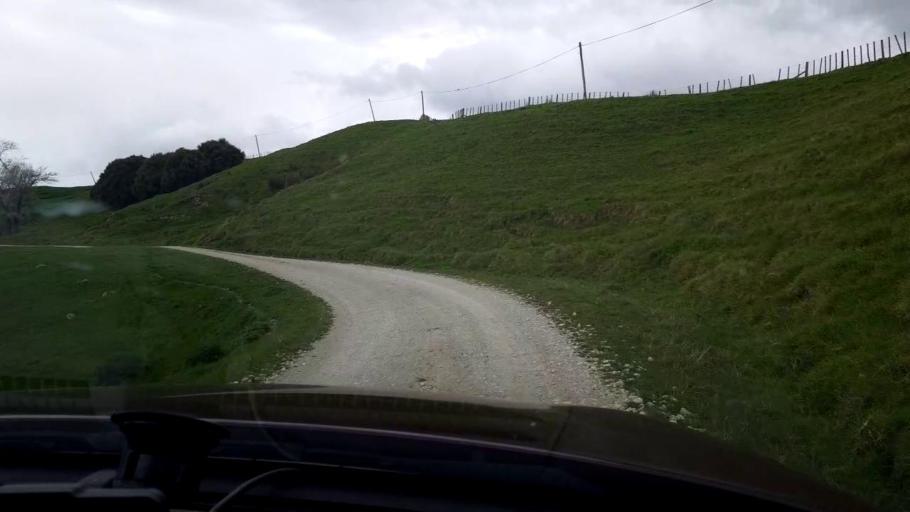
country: NZ
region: Gisborne
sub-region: Gisborne District
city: Gisborne
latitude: -38.3679
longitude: 177.9581
